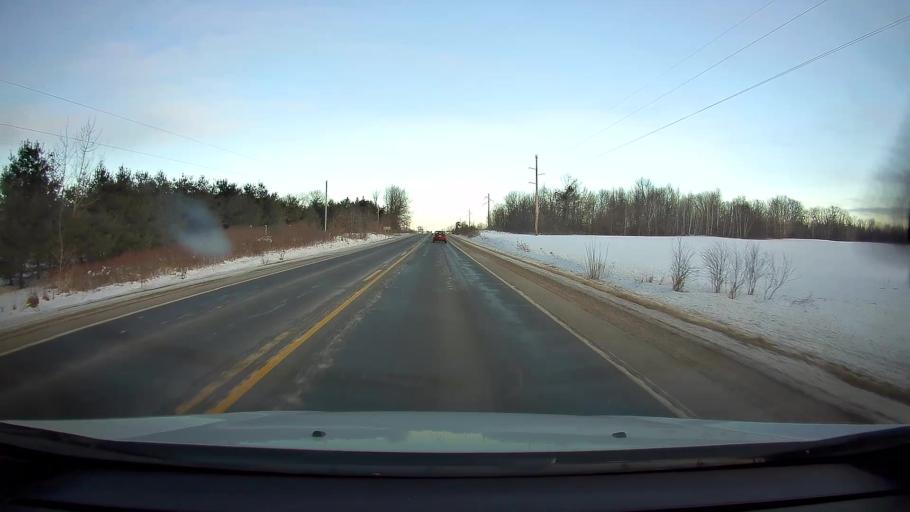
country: US
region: Wisconsin
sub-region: Barron County
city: Turtle Lake
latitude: 45.3604
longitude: -92.1668
